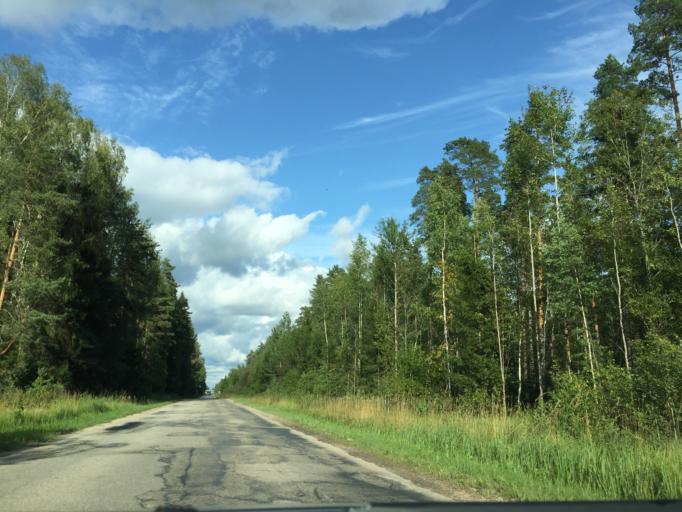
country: LV
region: Ogre
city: Ogre
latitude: 56.8351
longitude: 24.6564
